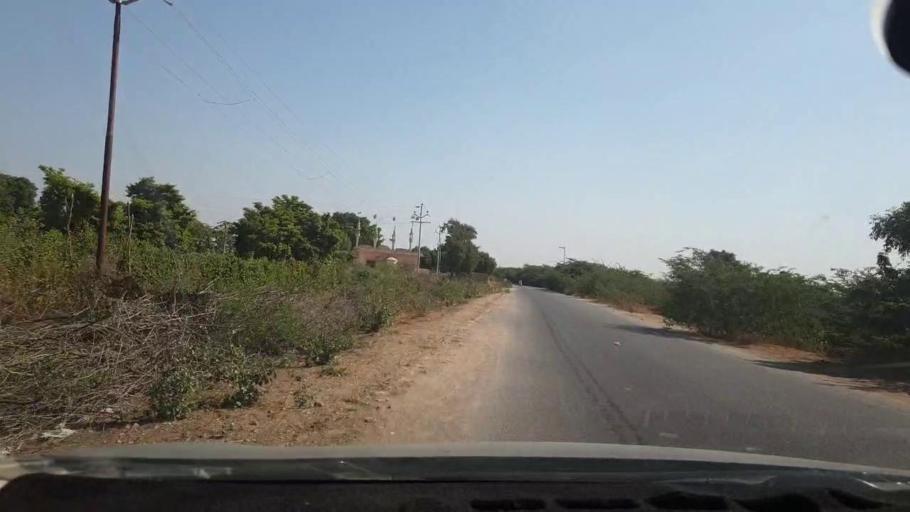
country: PK
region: Sindh
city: Malir Cantonment
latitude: 25.1401
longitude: 67.2061
